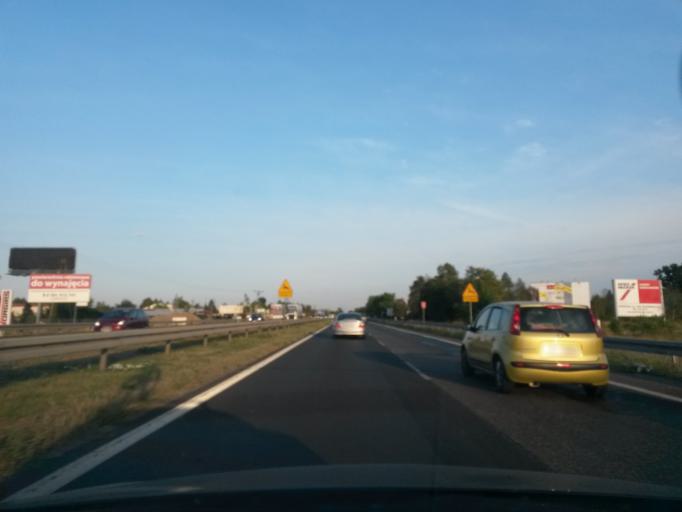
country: PL
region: Masovian Voivodeship
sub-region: Powiat warszawski zachodni
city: Dziekanow Lesny
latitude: 52.3545
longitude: 20.8447
